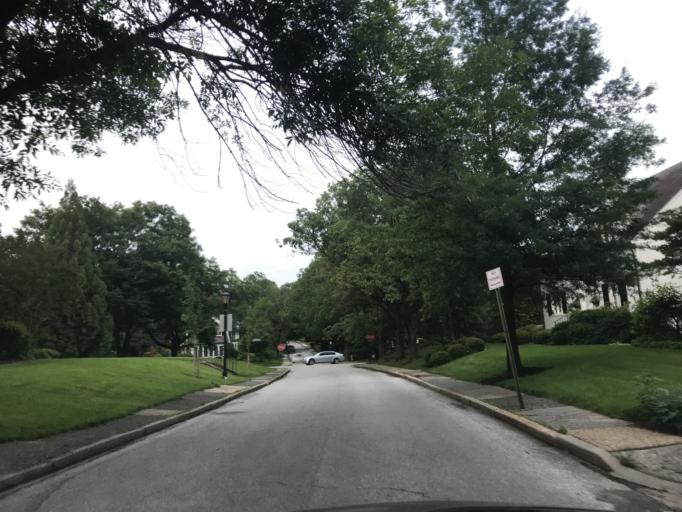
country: US
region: Maryland
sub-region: Baltimore County
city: Towson
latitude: 39.3605
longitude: -76.6179
